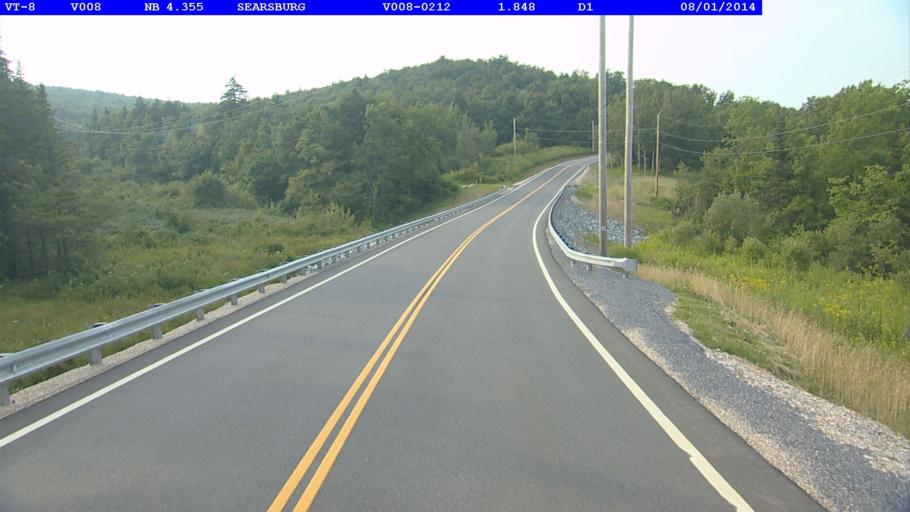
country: US
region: Vermont
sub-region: Windham County
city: Dover
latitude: 42.8832
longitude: -72.9727
